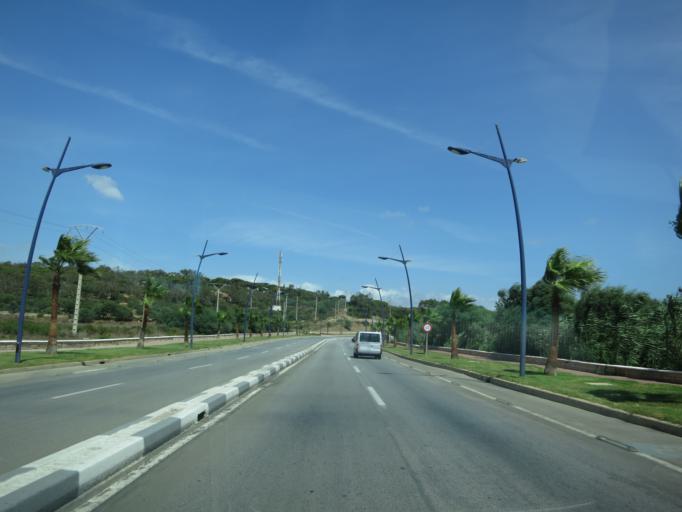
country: ES
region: Ceuta
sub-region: Ceuta
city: Ceuta
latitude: 35.7695
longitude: -5.3496
